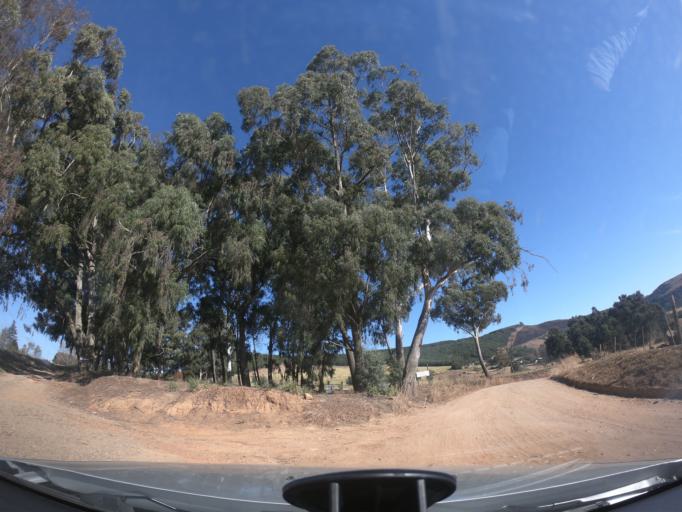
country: ZA
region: KwaZulu-Natal
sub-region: uMgungundlovu District Municipality
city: Impendle
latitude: -29.4226
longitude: 29.9085
